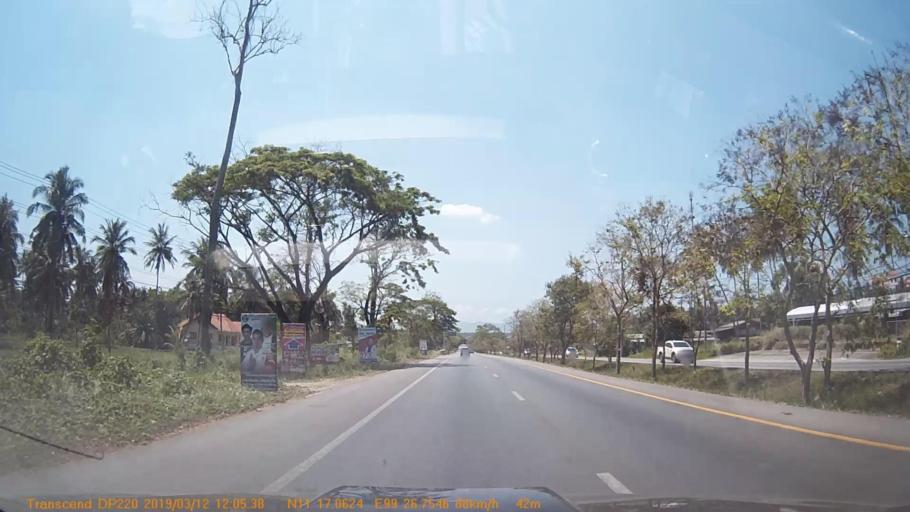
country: TH
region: Prachuap Khiri Khan
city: Bang Saphan
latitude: 11.2842
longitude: 99.4458
